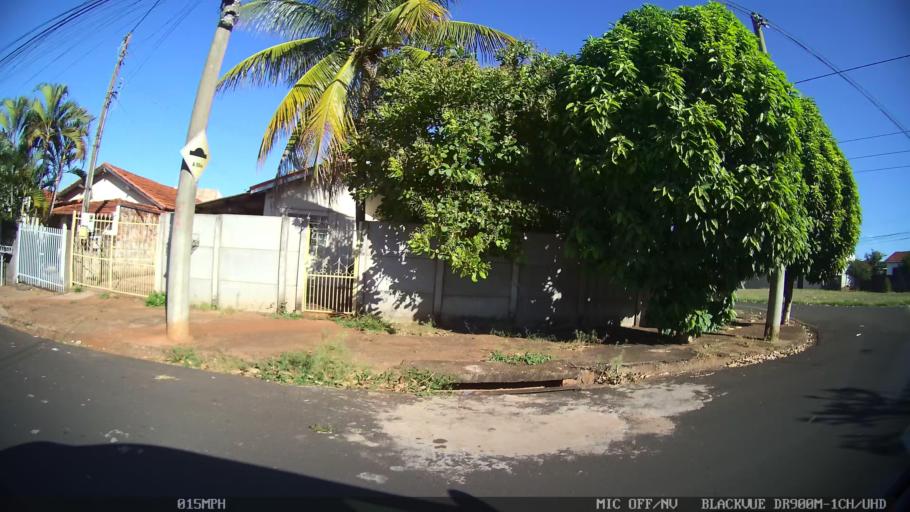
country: BR
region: Sao Paulo
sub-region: Olimpia
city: Olimpia
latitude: -20.7424
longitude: -48.8883
